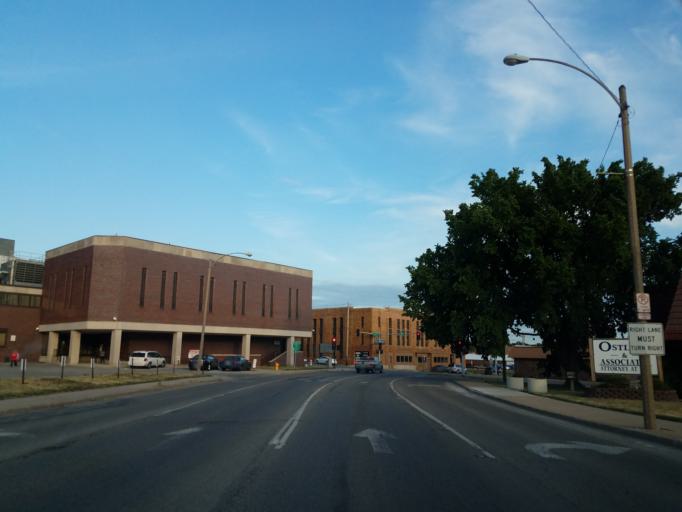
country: US
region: Illinois
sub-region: McLean County
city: Bloomington
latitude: 40.4777
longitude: -88.9951
